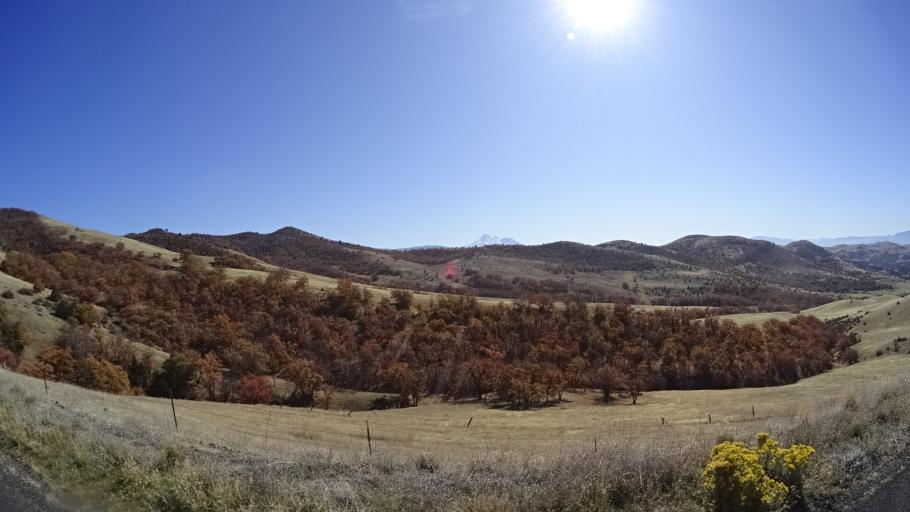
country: US
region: California
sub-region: Siskiyou County
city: Montague
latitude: 41.8239
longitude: -122.3413
